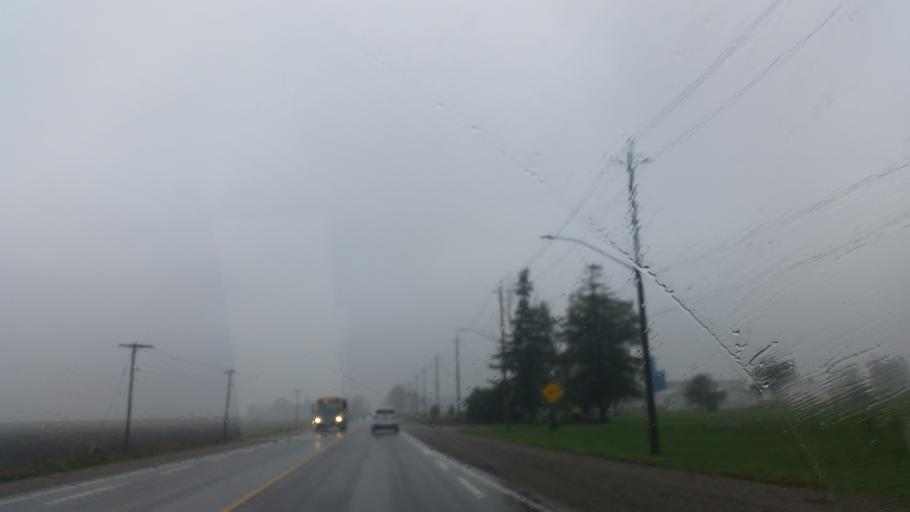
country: CA
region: Ontario
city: Stratford
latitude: 43.3439
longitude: -81.0061
